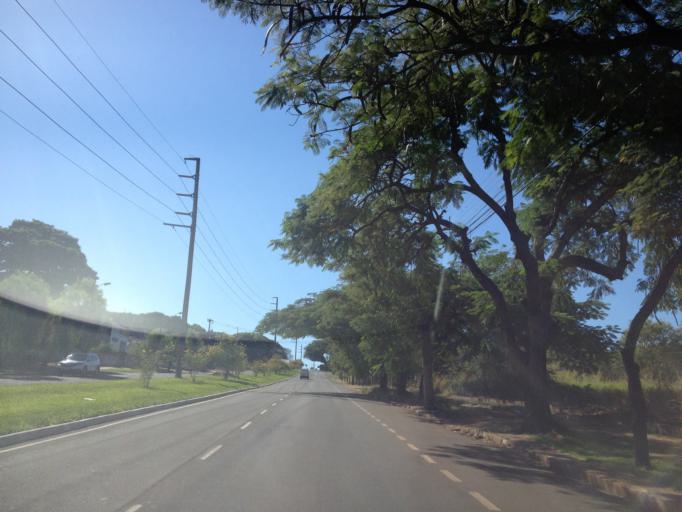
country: BR
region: Parana
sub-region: Maringa
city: Maringa
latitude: -23.4481
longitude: -51.9372
